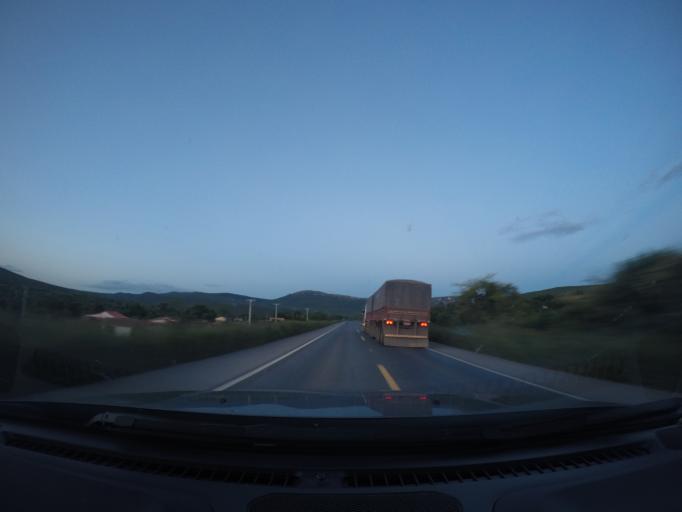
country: BR
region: Bahia
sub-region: Seabra
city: Seabra
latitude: -12.4811
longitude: -41.7191
